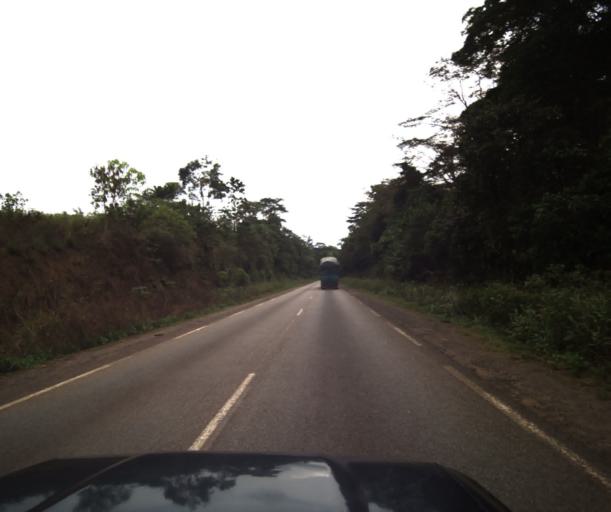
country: CM
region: Littoral
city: Edea
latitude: 3.8214
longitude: 10.3781
